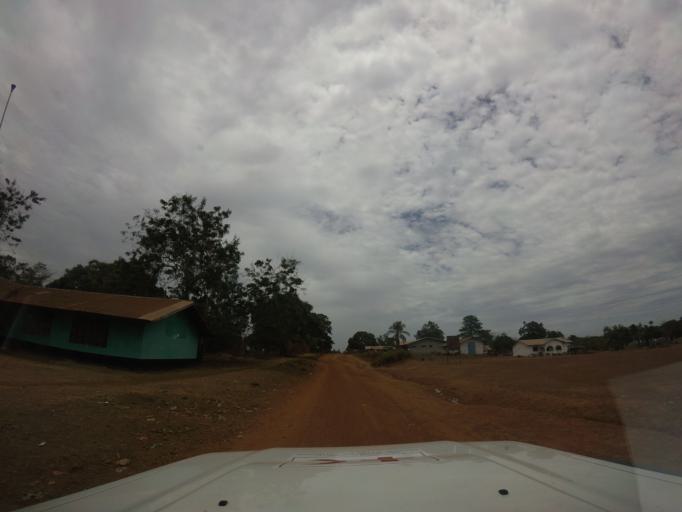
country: LR
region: Grand Cape Mount
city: Robertsport
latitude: 6.9707
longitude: -11.3109
